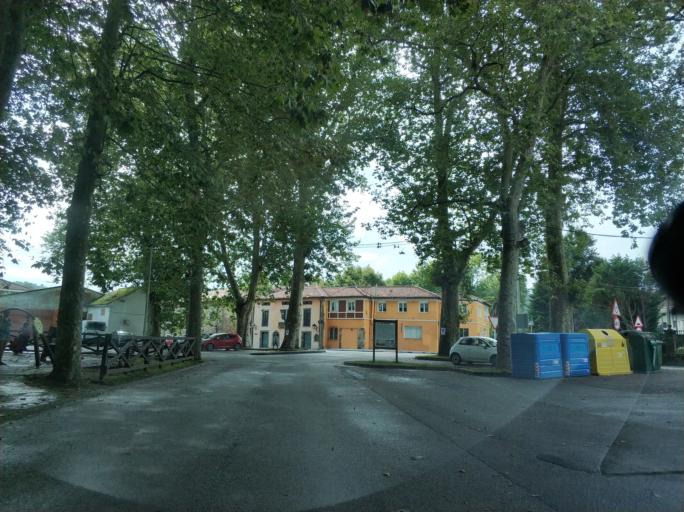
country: ES
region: Cantabria
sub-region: Provincia de Cantabria
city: Miengo
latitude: 43.4028
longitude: -3.9495
